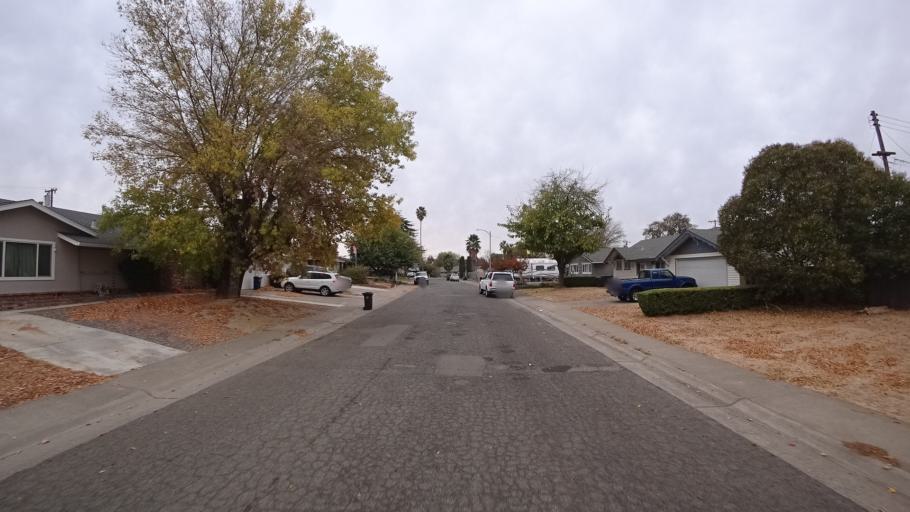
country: US
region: California
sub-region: Sacramento County
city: Citrus Heights
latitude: 38.6951
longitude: -121.2955
